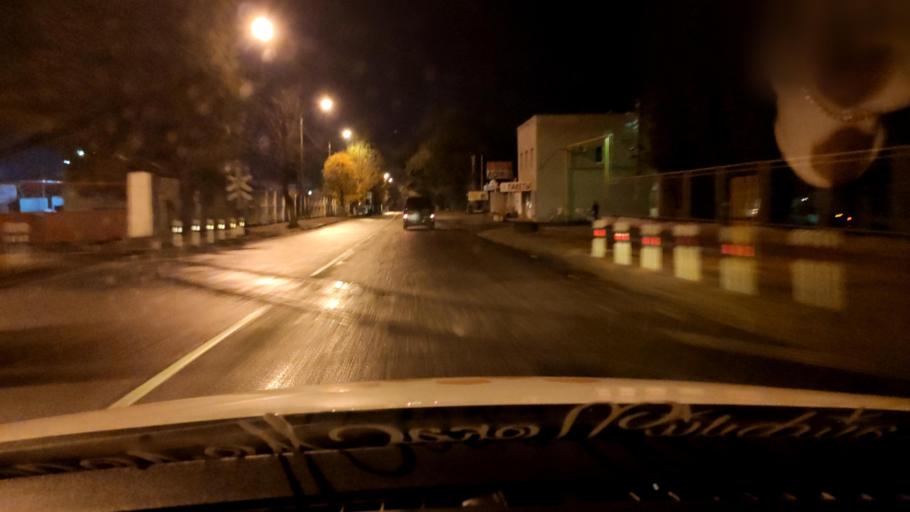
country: RU
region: Voronezj
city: Voronezh
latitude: 51.6646
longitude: 39.1451
